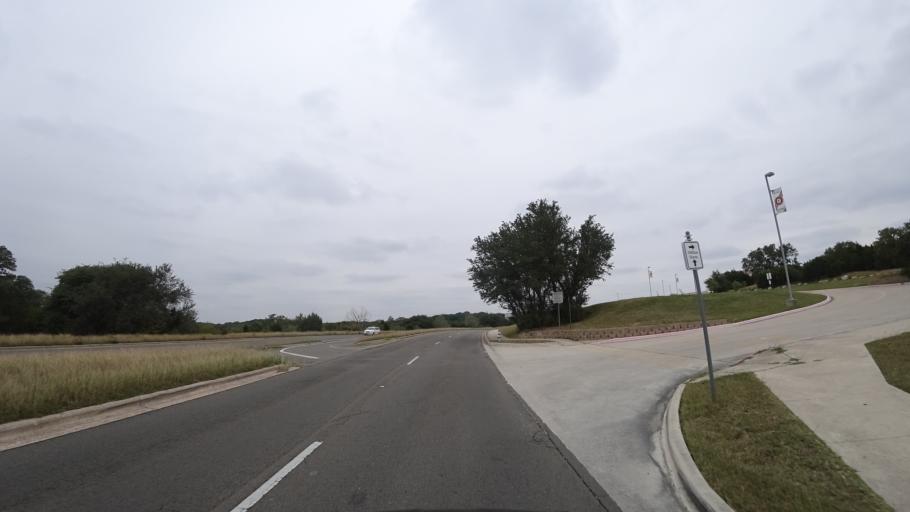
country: US
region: Texas
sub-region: Travis County
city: Shady Hollow
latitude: 30.2116
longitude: -97.8922
